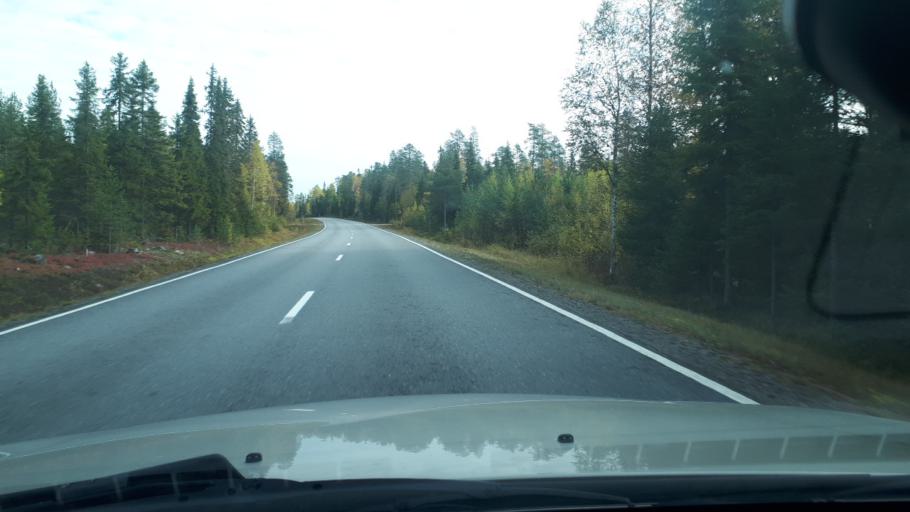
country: FI
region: Northern Ostrobothnia
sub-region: Oulu
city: Yli-Ii
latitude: 65.9277
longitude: 25.8507
